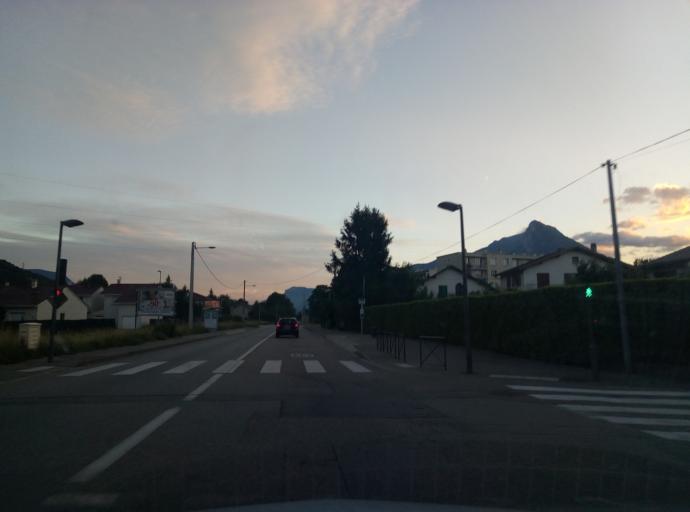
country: FR
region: Rhone-Alpes
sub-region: Departement de l'Isere
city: Sassenage
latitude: 45.2146
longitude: 5.6613
